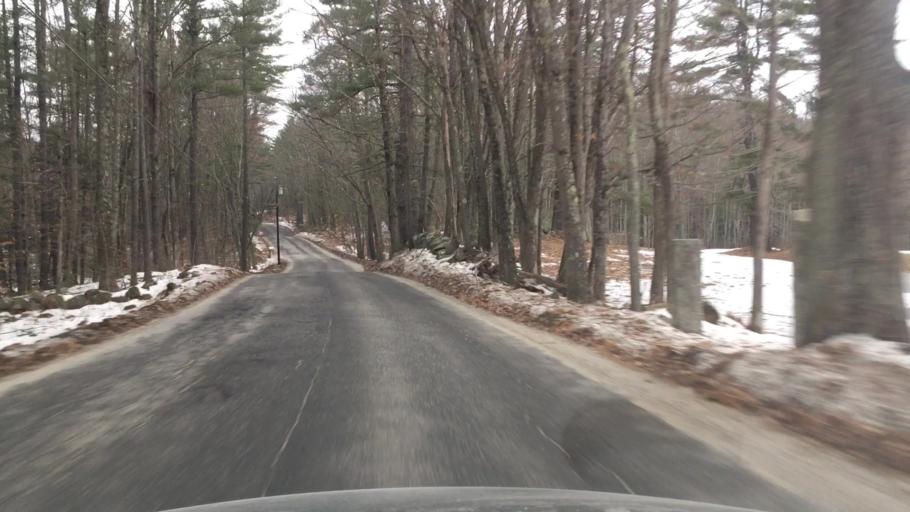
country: US
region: New Hampshire
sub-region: Hillsborough County
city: New Boston
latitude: 43.0075
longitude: -71.6690
